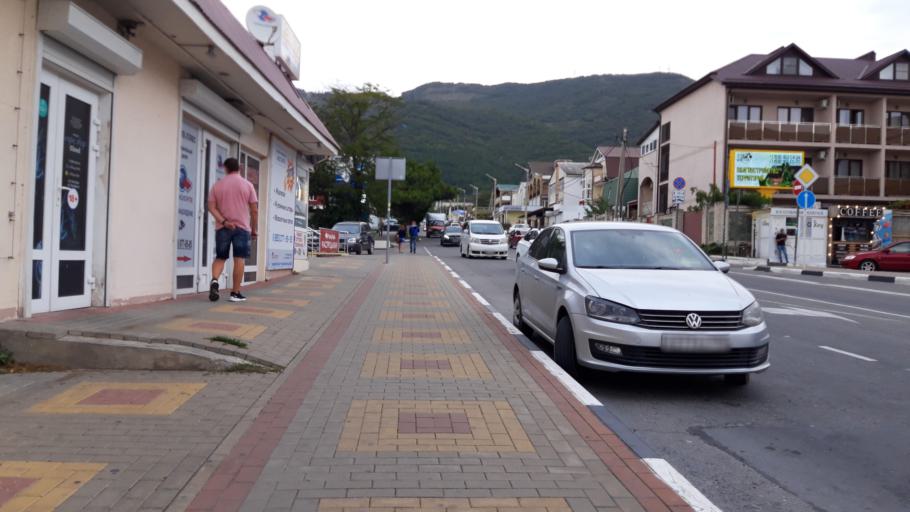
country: RU
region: Krasnodarskiy
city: Gelendzhik
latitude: 44.5680
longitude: 38.0895
